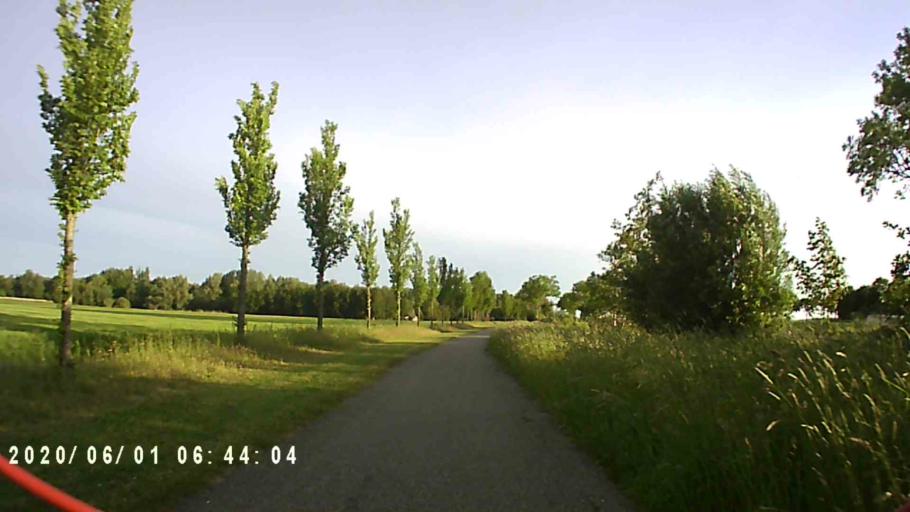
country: NL
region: Friesland
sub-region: Gemeente Kollumerland en Nieuwkruisland
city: Kollum
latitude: 53.3000
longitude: 6.1498
